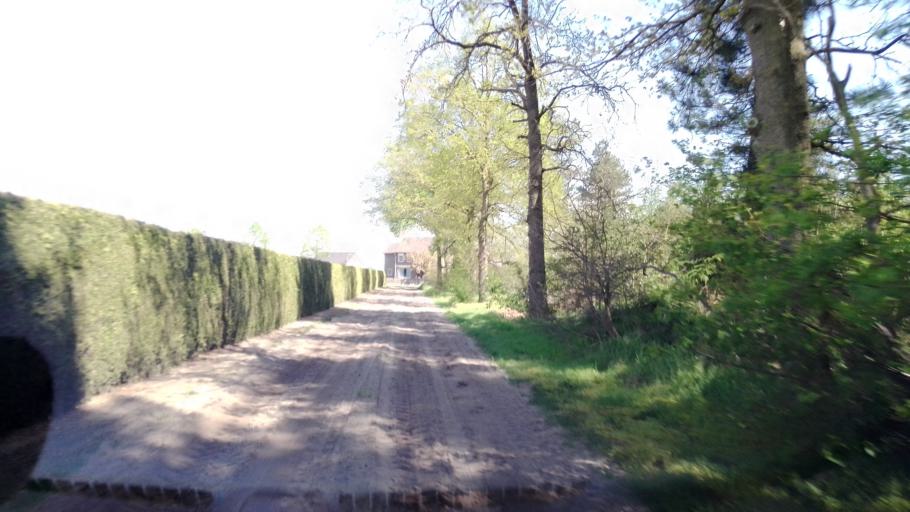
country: NL
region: Limburg
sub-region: Gemeente Venlo
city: Arcen
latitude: 51.4553
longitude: 6.1203
